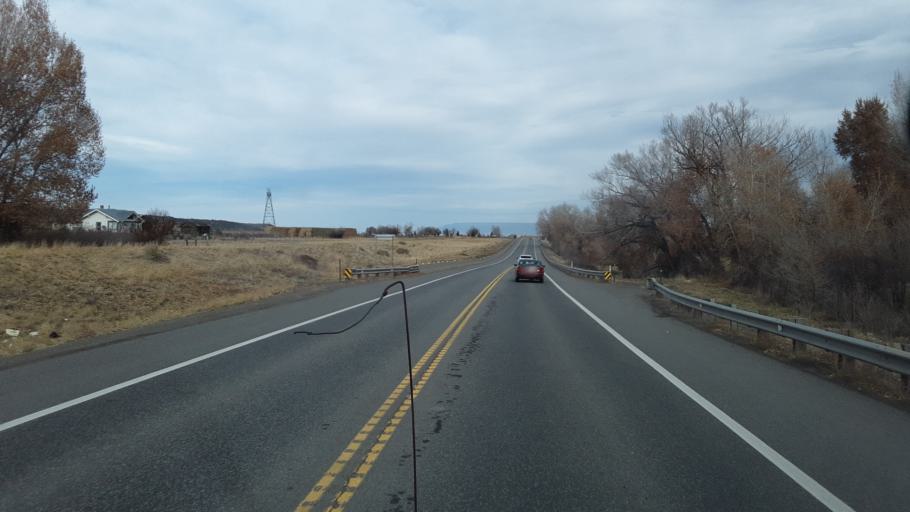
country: US
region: Colorado
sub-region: Montrose County
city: Montrose
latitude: 38.3337
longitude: -107.7841
